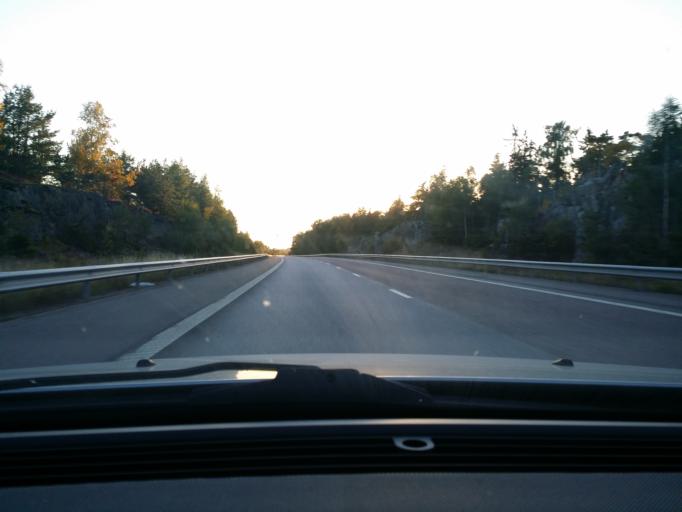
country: SE
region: Uppsala
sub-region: Habo Kommun
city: Balsta
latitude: 59.5928
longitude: 17.4835
